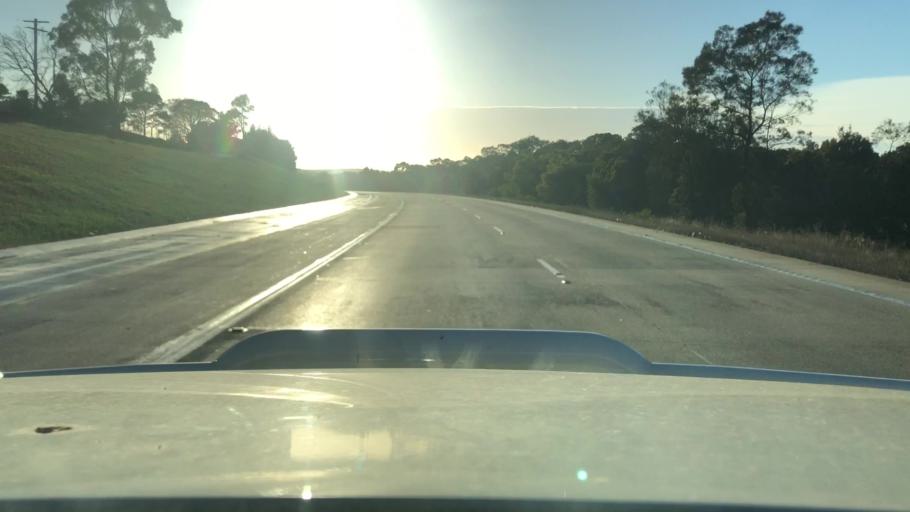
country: AU
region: New South Wales
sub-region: Wingecarribee
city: Bundanoon
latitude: -34.6914
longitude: 150.0356
